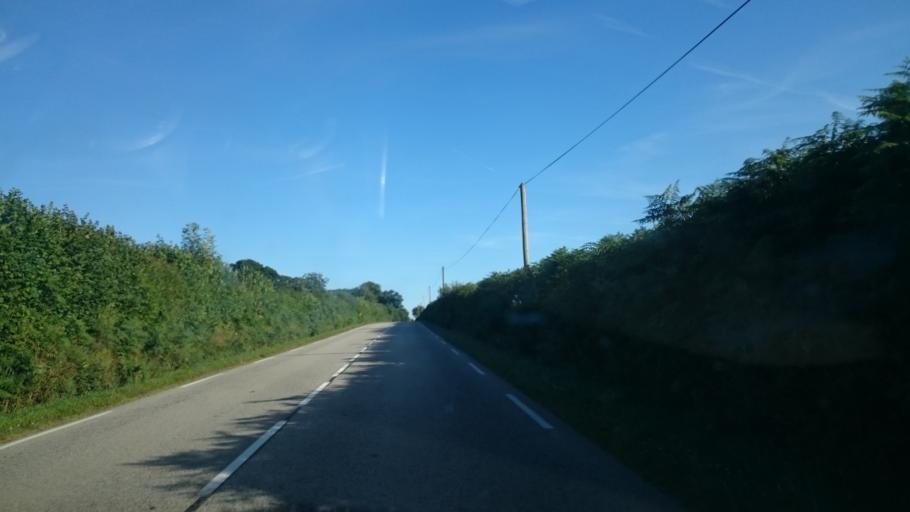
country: FR
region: Lower Normandy
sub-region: Departement de la Manche
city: Martinvast
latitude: 49.5625
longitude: -1.6900
